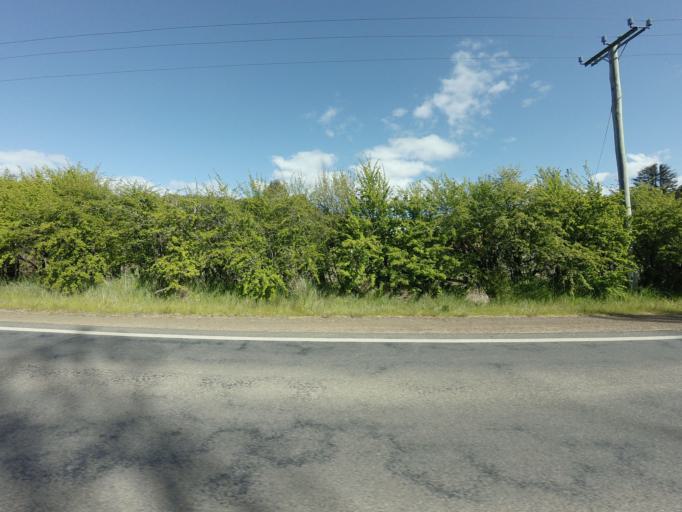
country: AU
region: Tasmania
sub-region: Derwent Valley
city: New Norfolk
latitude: -42.7783
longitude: 147.0450
